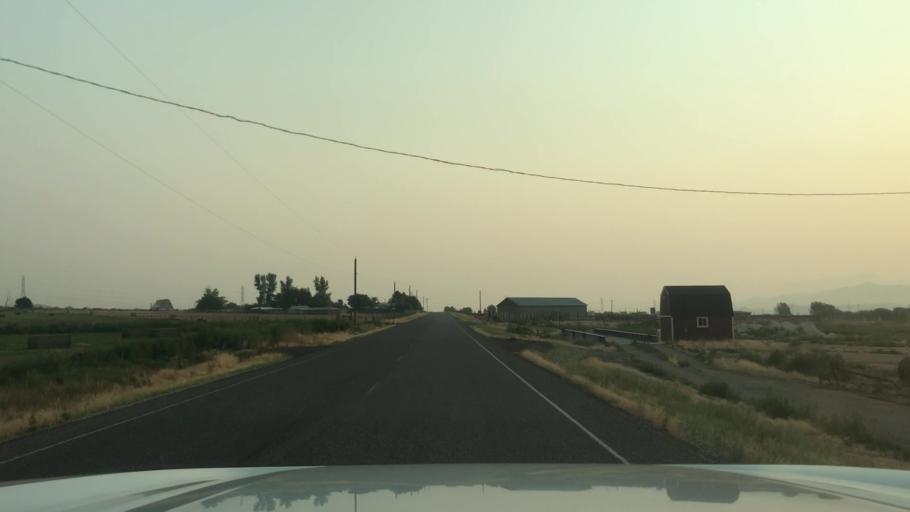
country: US
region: Utah
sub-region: Sevier County
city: Aurora
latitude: 38.8864
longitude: -111.9575
